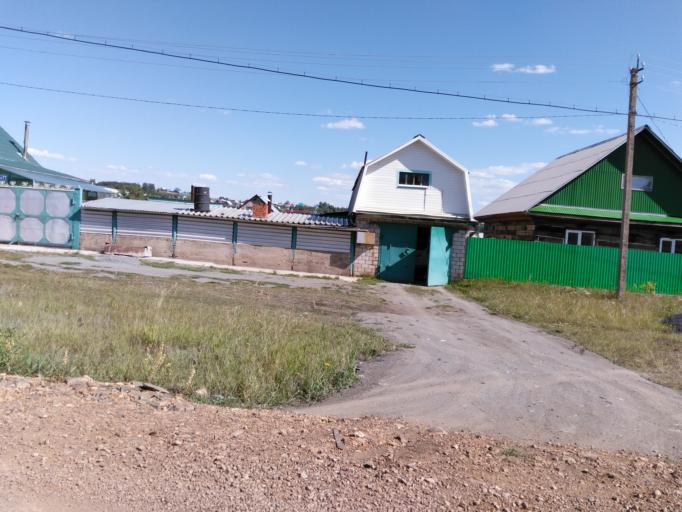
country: RU
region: Bashkortostan
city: Uchaly
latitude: 54.2928
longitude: 59.3613
